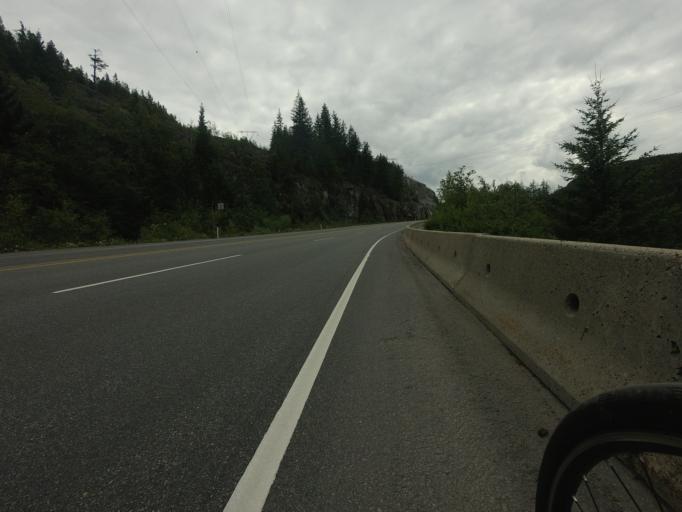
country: CA
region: British Columbia
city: Whistler
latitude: 49.9265
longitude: -123.1637
